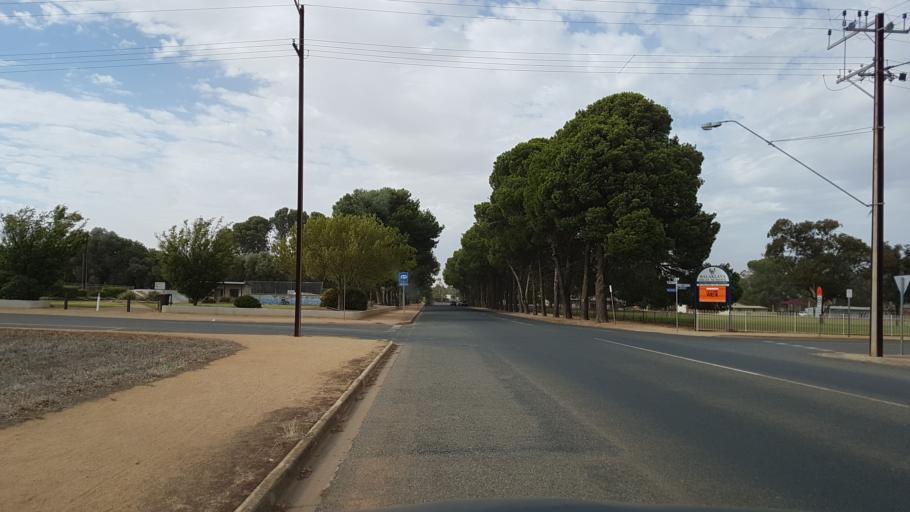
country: AU
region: South Australia
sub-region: Wakefield
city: Balaklava
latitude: -34.1487
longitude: 138.4162
